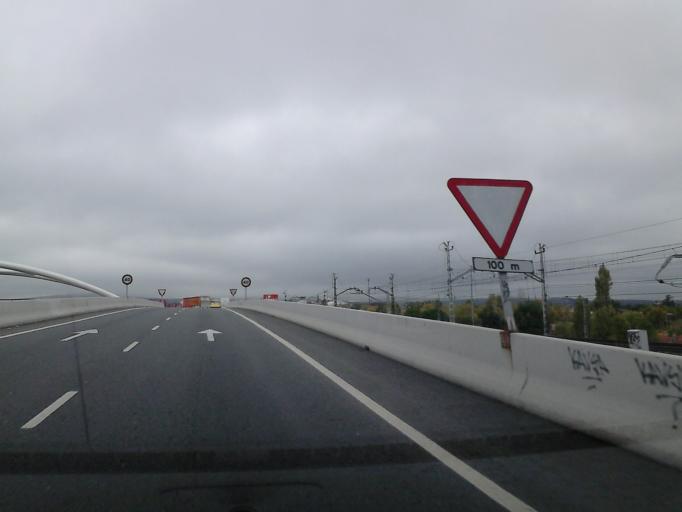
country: ES
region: Madrid
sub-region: Provincia de Madrid
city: Las Matas
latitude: 40.5461
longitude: -3.8941
